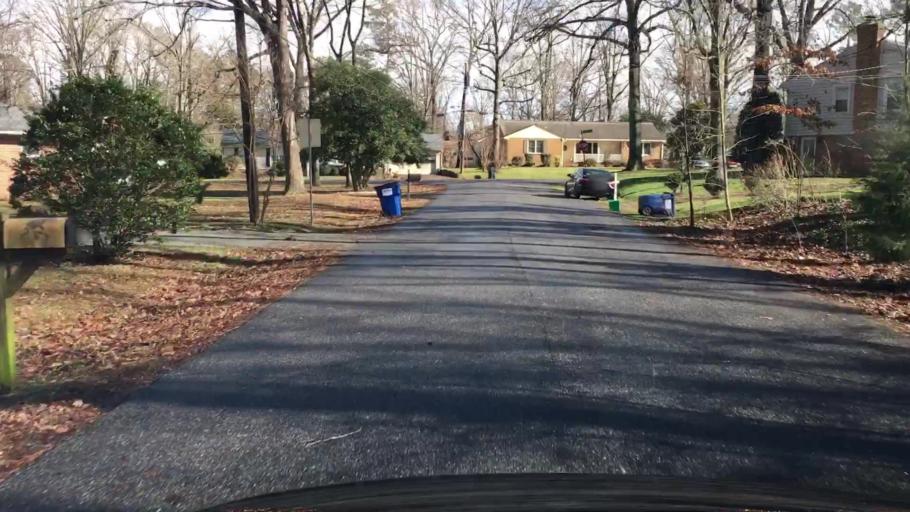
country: US
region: Virginia
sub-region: Chesterfield County
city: Bon Air
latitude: 37.5314
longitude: -77.5835
